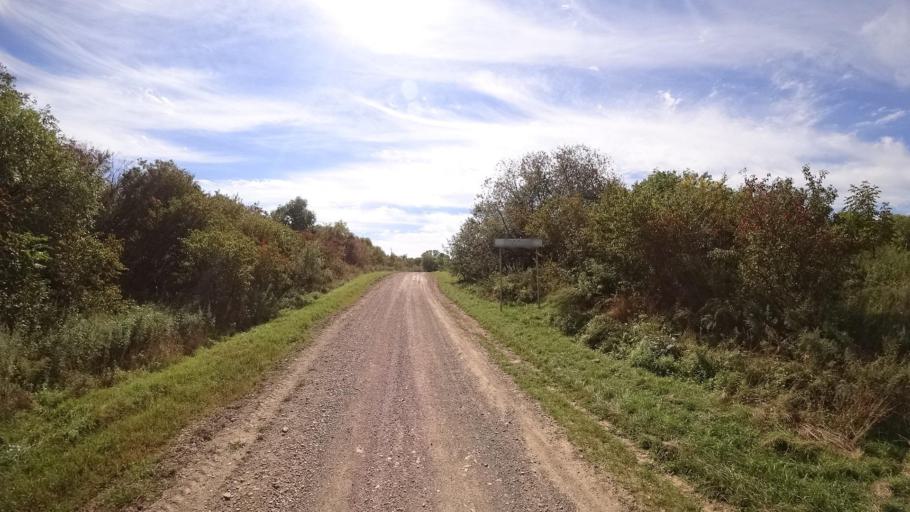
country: RU
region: Primorskiy
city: Kirovskiy
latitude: 44.7606
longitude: 133.6109
